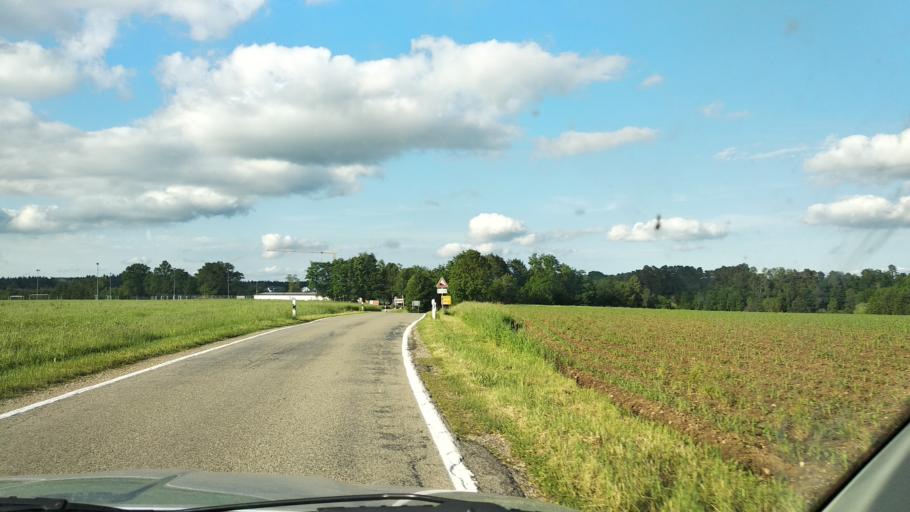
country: DE
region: Baden-Wuerttemberg
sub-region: Tuebingen Region
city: Rot an der Rot
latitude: 47.9696
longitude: 10.0450
